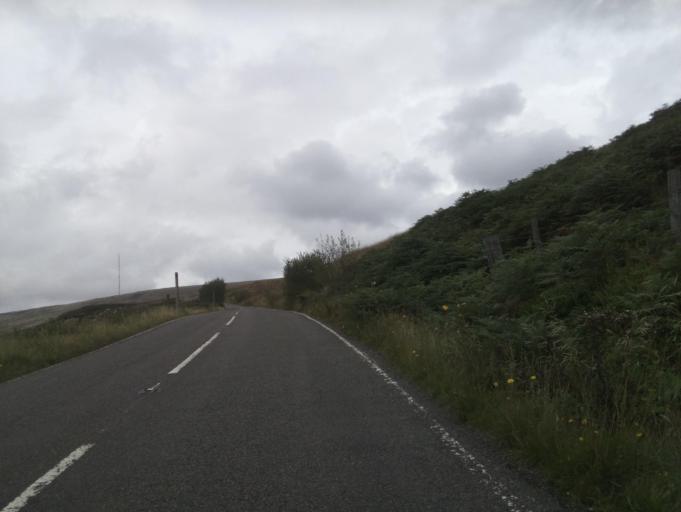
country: GB
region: England
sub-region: Kirklees
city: Meltham
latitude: 53.5117
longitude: -1.8528
